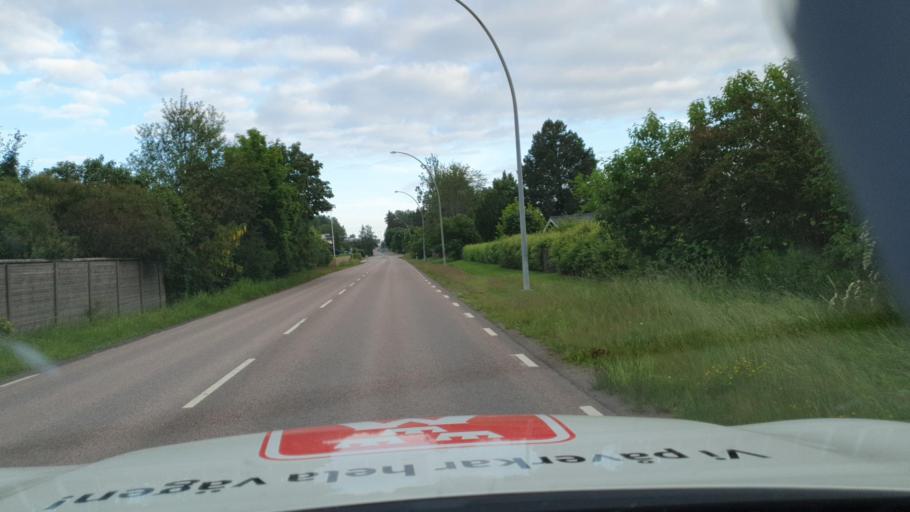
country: SE
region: Vaermland
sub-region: Karlstads Kommun
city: Karlstad
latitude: 59.4012
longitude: 13.5136
